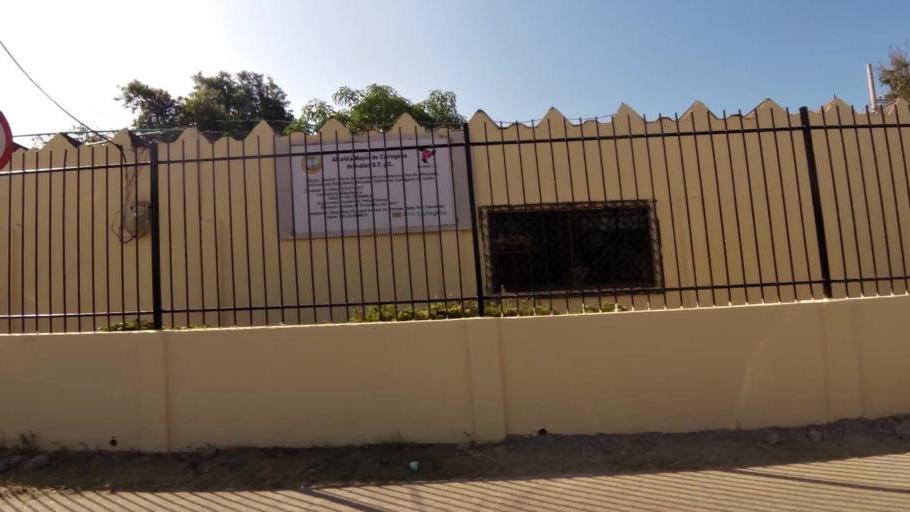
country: CO
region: Bolivar
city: Cartagena
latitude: 10.3806
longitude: -75.4747
